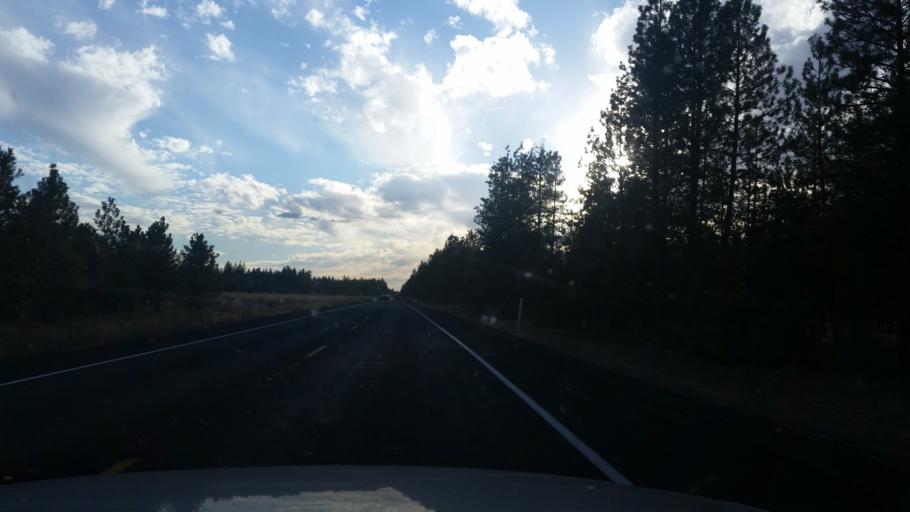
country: US
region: Washington
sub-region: Spokane County
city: Cheney
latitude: 47.4633
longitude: -117.6756
